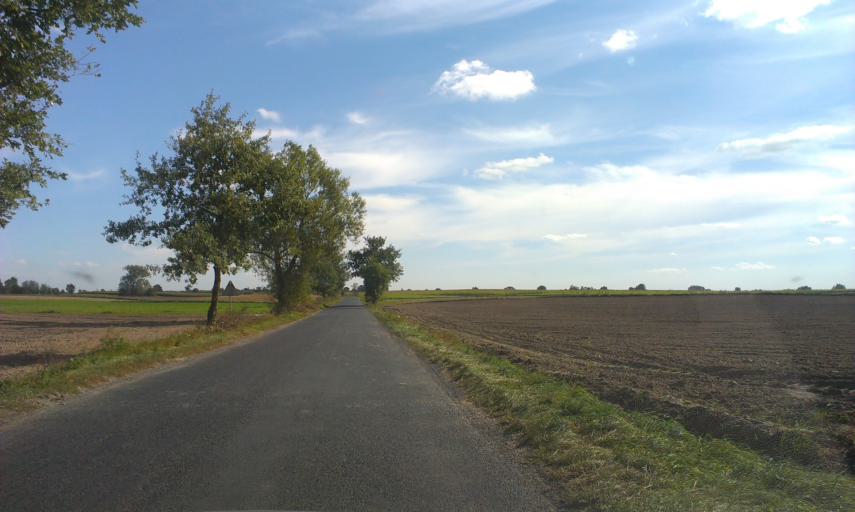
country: PL
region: Greater Poland Voivodeship
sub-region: Powiat pilski
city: Lobzenica
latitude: 53.2821
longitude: 17.1891
